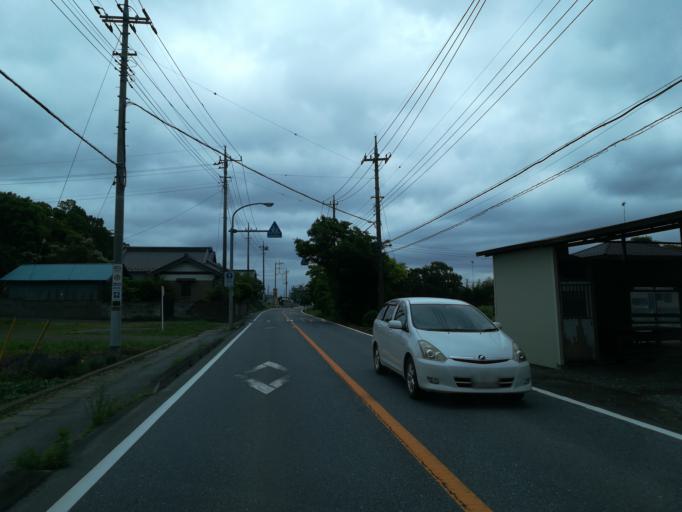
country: JP
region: Ibaraki
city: Tsukuba
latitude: 36.1893
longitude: 140.0792
